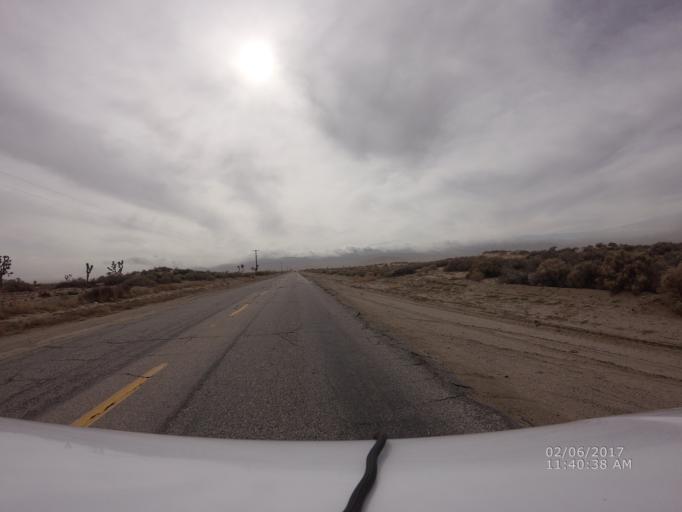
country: US
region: California
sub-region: Los Angeles County
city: Lake Los Angeles
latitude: 34.6146
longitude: -117.7027
